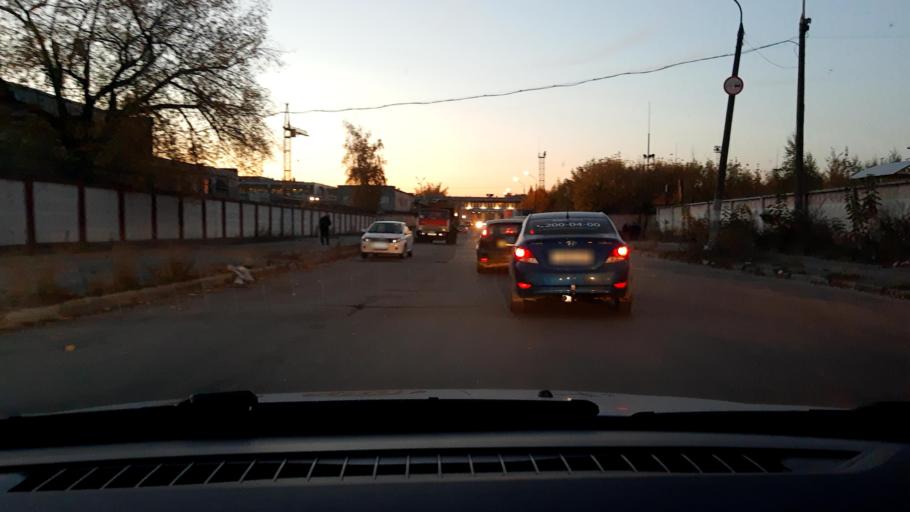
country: RU
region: Nizjnij Novgorod
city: Burevestnik
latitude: 56.2364
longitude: 43.8844
